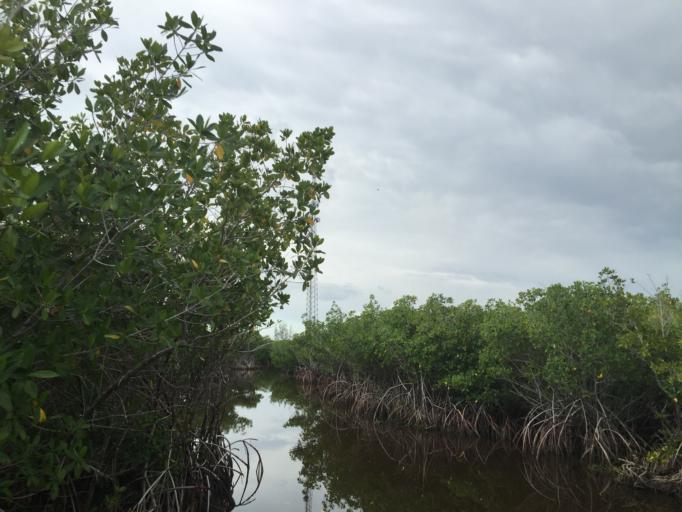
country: US
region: Florida
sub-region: Collier County
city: Marco
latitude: 25.9116
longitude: -81.3700
